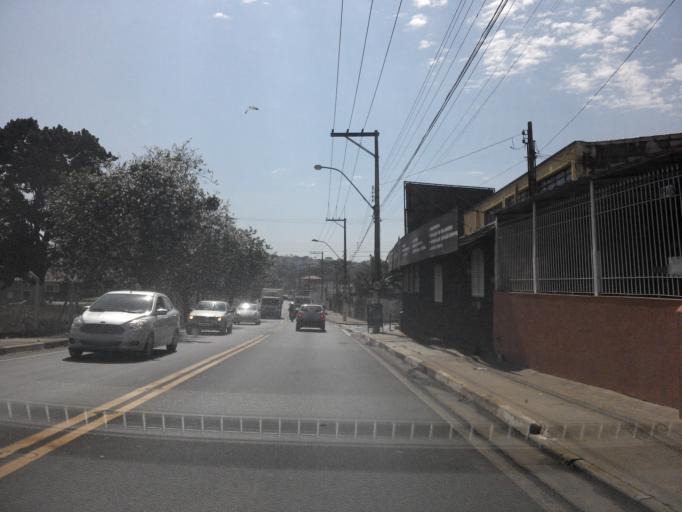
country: BR
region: Sao Paulo
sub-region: Hortolandia
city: Hortolandia
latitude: -22.8649
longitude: -47.2245
